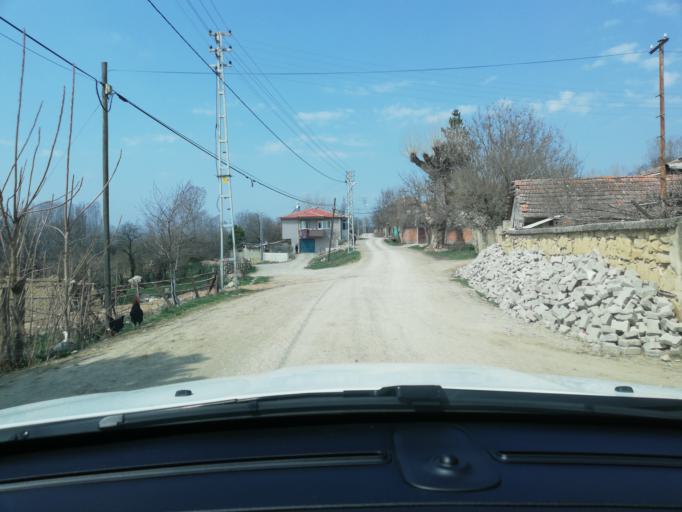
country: TR
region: Kastamonu
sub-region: Cide
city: Kastamonu
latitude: 41.4585
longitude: 33.7601
